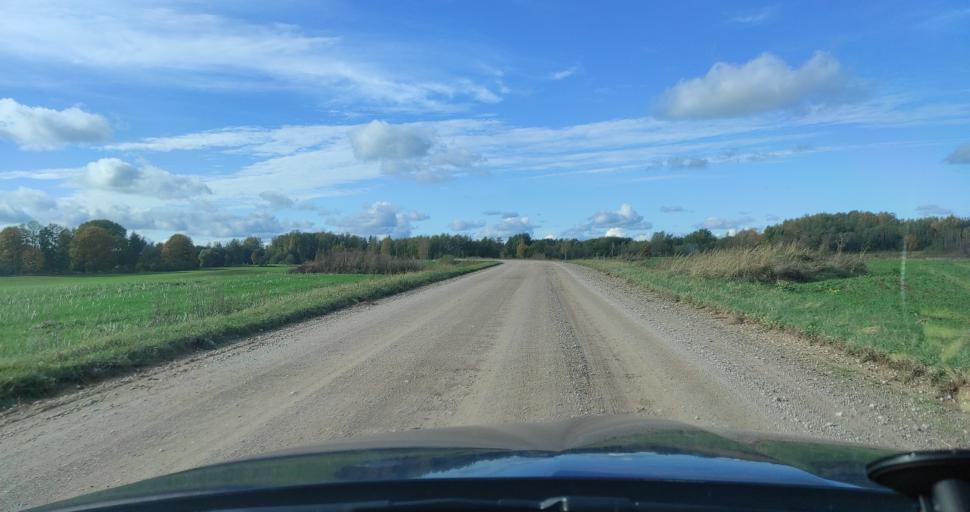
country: LV
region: Jaunpils
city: Jaunpils
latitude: 56.8307
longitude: 22.9879
